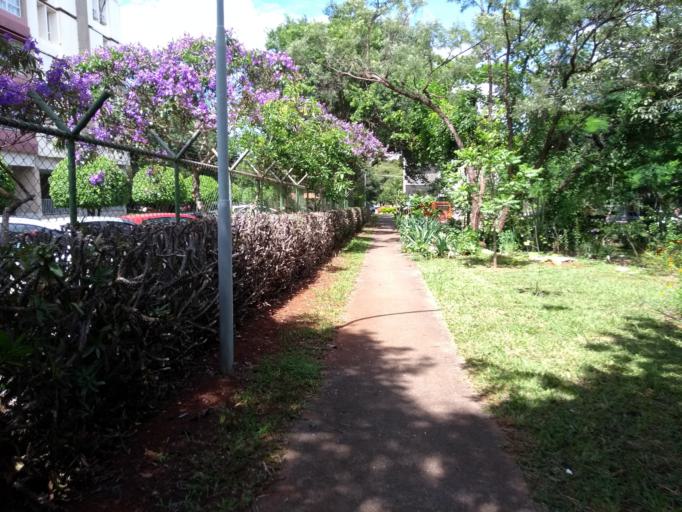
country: BR
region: Federal District
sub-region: Brasilia
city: Brasilia
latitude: -15.8055
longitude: -47.9456
